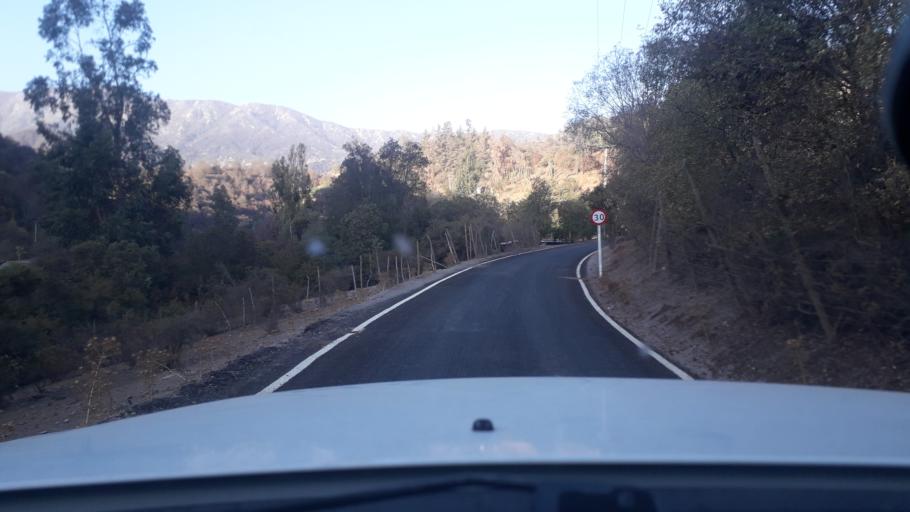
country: CL
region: Valparaiso
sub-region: Provincia de Marga Marga
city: Limache
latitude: -33.0462
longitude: -71.0600
